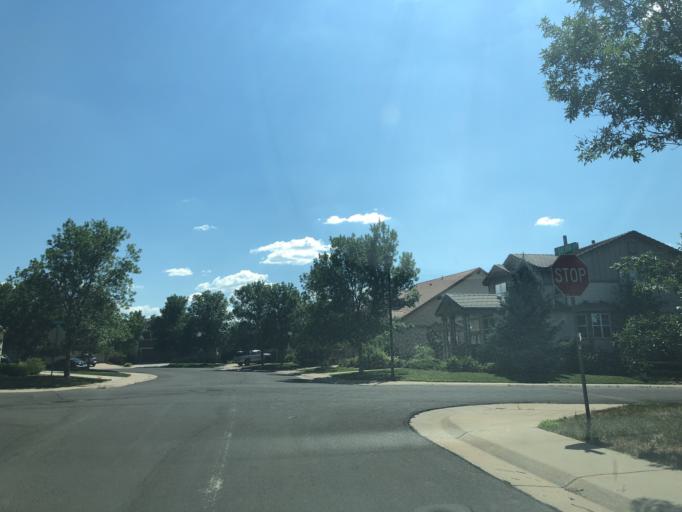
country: US
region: Colorado
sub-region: Arapahoe County
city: Dove Valley
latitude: 39.6045
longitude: -104.7842
